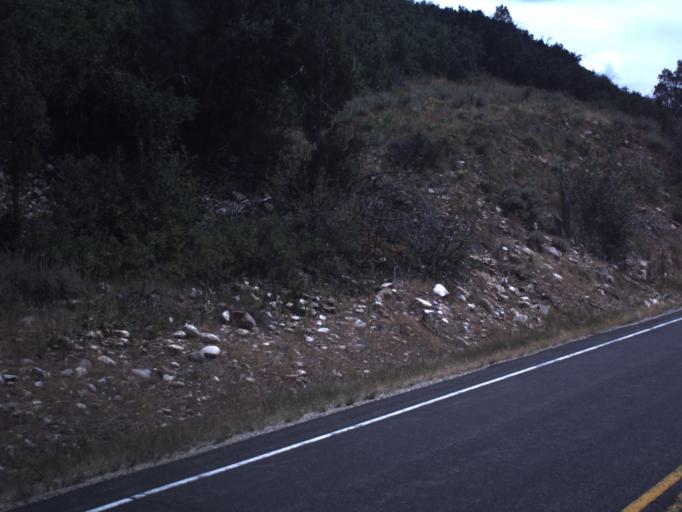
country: US
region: Utah
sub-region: Summit County
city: Francis
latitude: 40.5606
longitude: -111.1813
